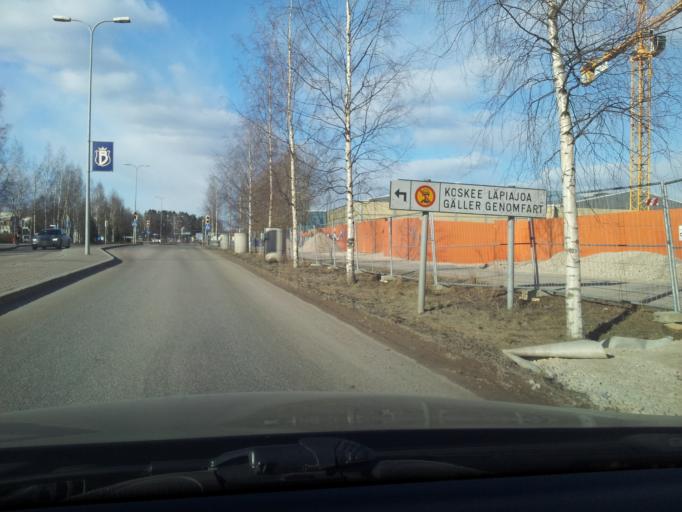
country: FI
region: Uusimaa
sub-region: Helsinki
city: Koukkuniemi
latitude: 60.1740
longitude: 24.7793
